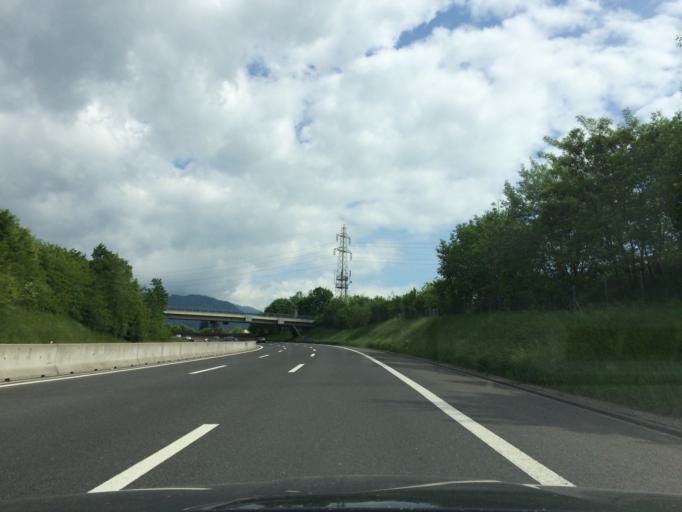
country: CH
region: Vaud
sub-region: Riviera-Pays-d'Enhaut District
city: Blonay
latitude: 46.4806
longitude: 6.8769
